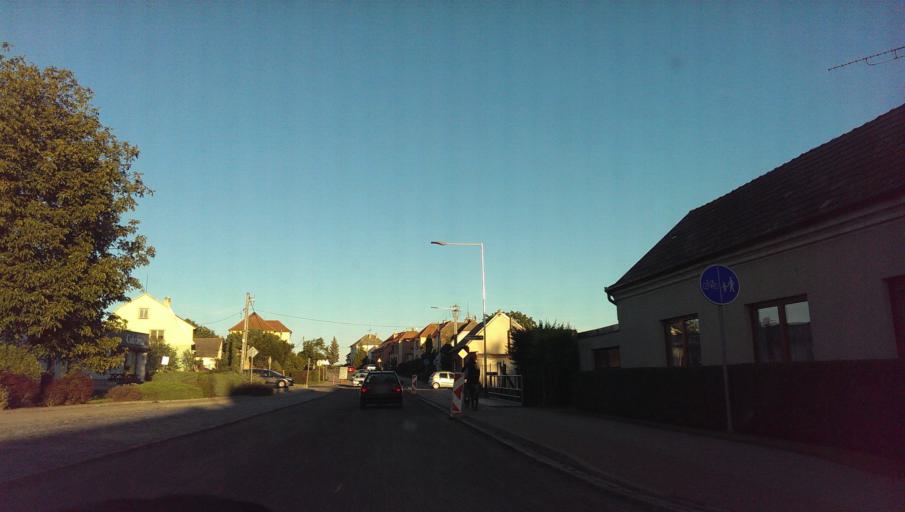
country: CZ
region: Zlin
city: Zlechov
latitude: 49.0738
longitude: 17.3914
